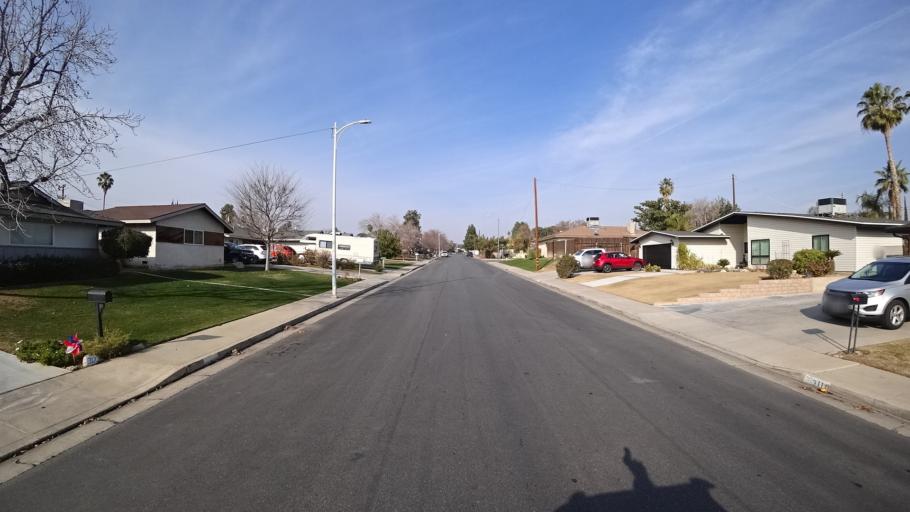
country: US
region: California
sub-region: Kern County
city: Oildale
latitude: 35.4024
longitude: -118.9476
